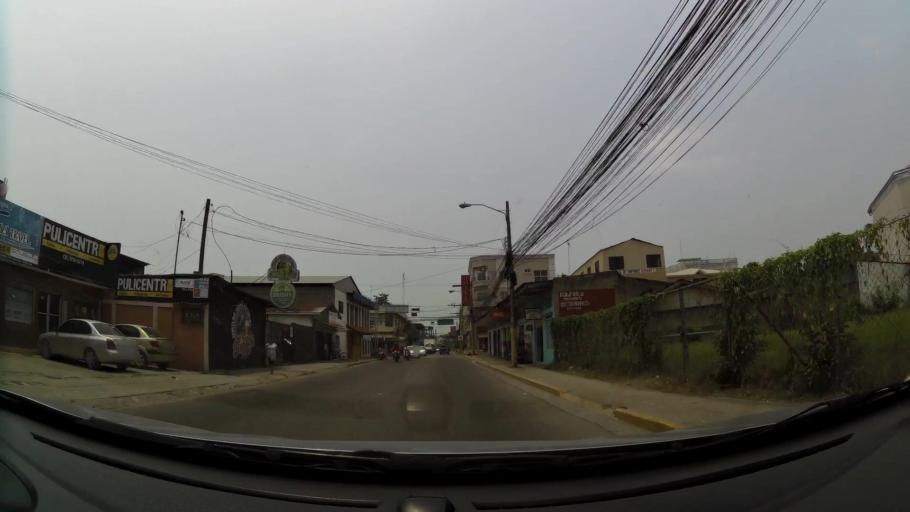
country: HN
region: Yoro
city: El Progreso
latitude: 15.3998
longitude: -87.8096
